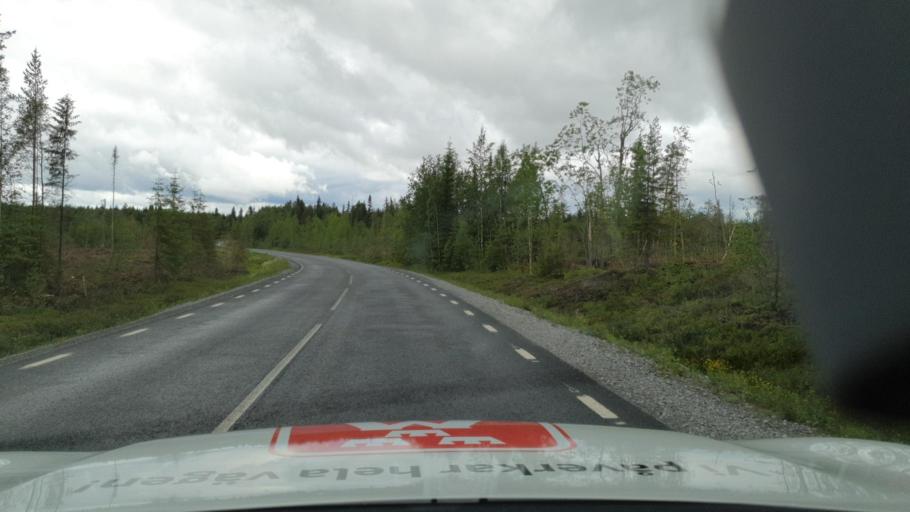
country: SE
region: Vaesterbotten
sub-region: Dorotea Kommun
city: Dorotea
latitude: 64.2458
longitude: 16.5340
